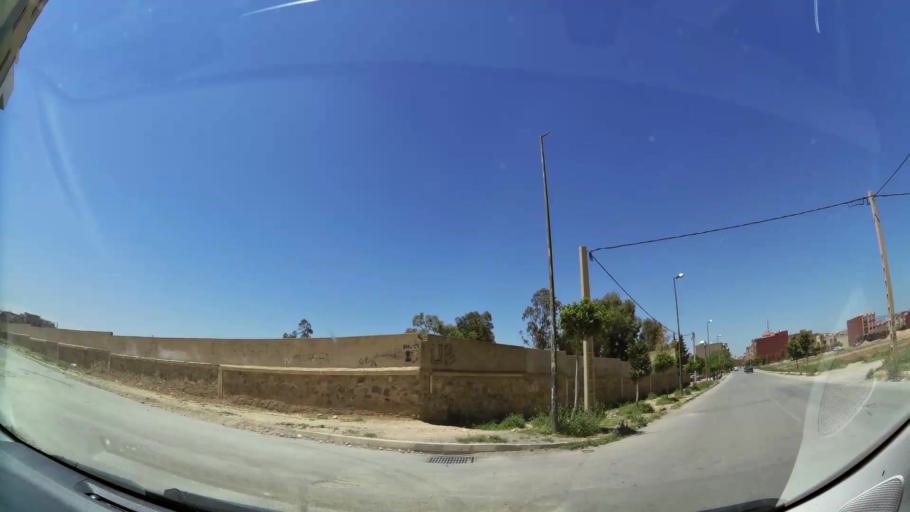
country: MA
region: Oriental
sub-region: Oujda-Angad
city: Oujda
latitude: 34.6701
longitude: -1.8799
